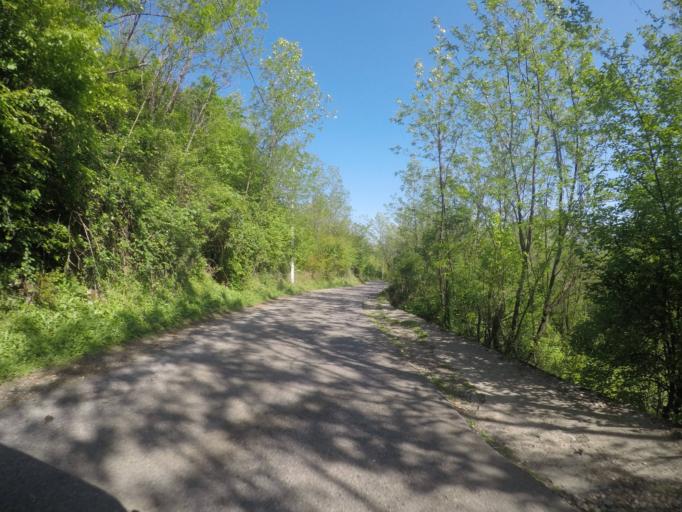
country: ME
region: Danilovgrad
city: Danilovgrad
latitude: 42.5372
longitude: 19.0904
